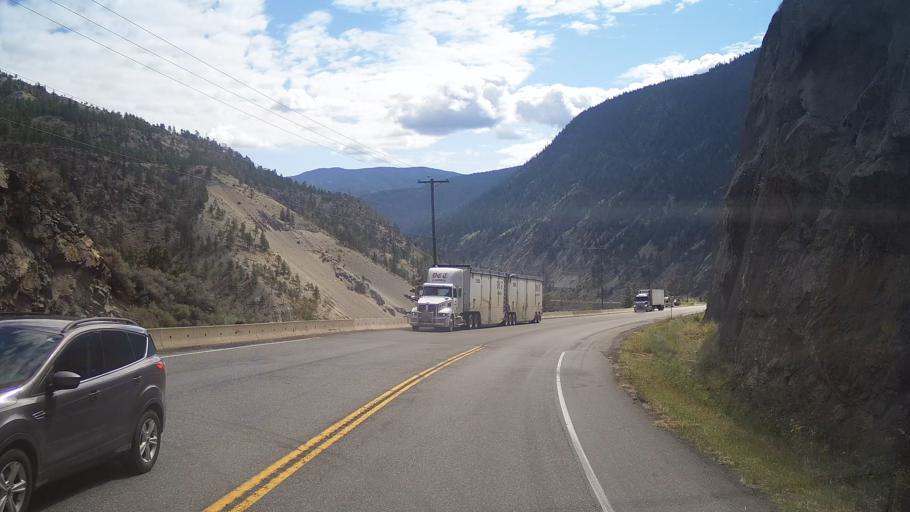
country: CA
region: British Columbia
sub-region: Thompson-Nicola Regional District
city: Ashcroft
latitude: 50.2579
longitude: -121.4616
